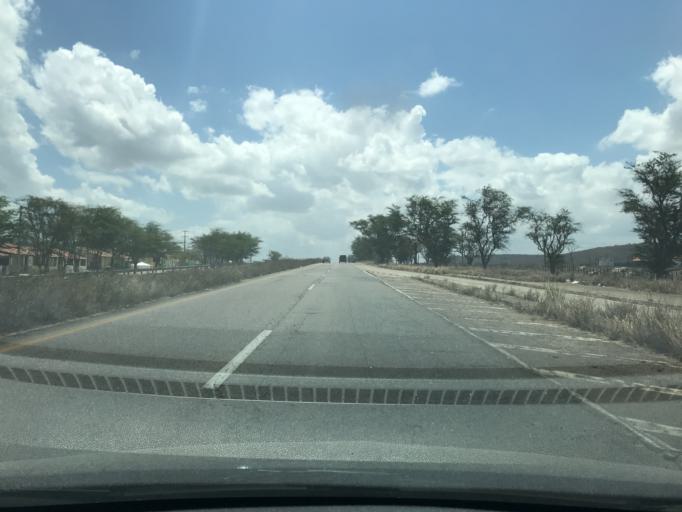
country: BR
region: Pernambuco
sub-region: Bezerros
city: Bezerros
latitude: -8.2970
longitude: -35.8669
